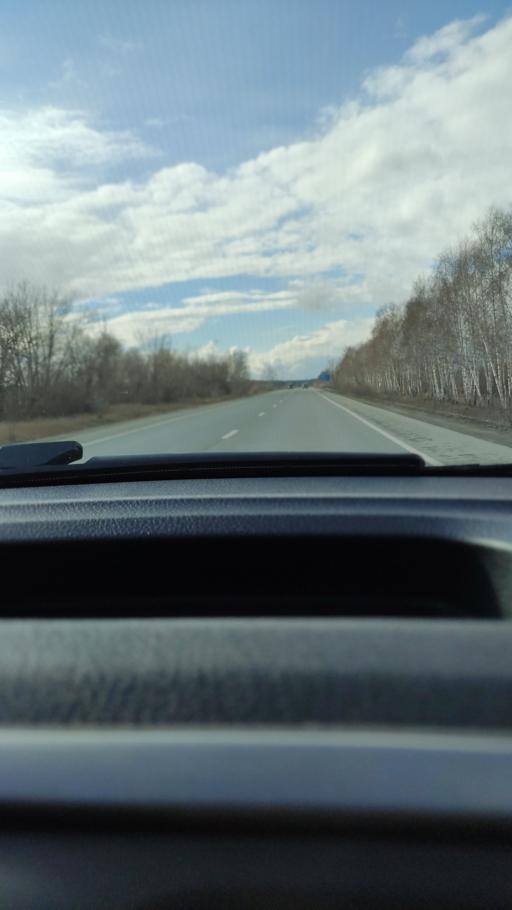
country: RU
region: Samara
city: Kurumoch
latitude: 53.4877
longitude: 50.0017
